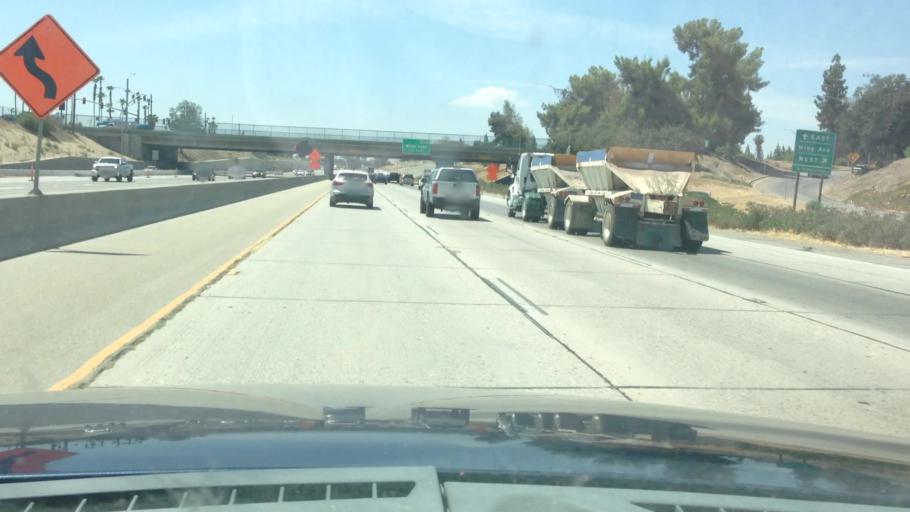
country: US
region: California
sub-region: Kern County
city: Bakersfield
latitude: 35.3411
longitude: -119.0396
